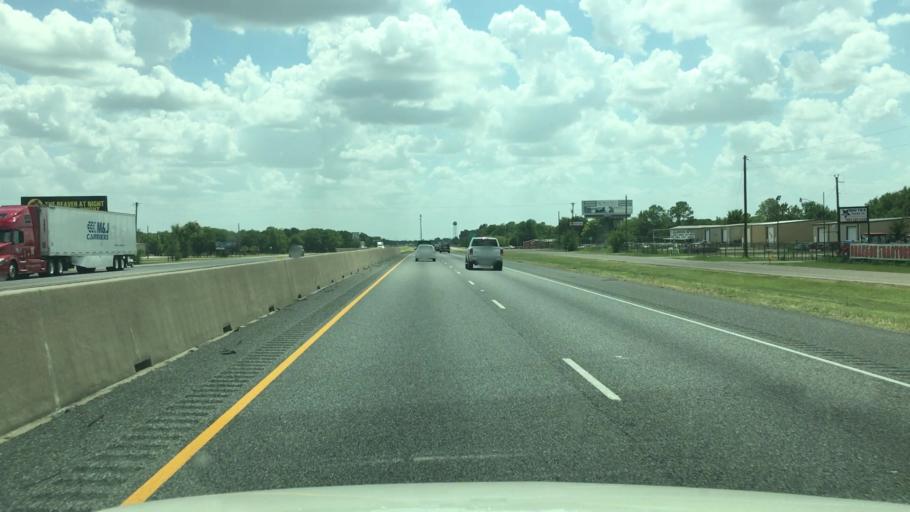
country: US
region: Texas
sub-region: Hunt County
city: Caddo Mills
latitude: 33.0329
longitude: -96.1888
